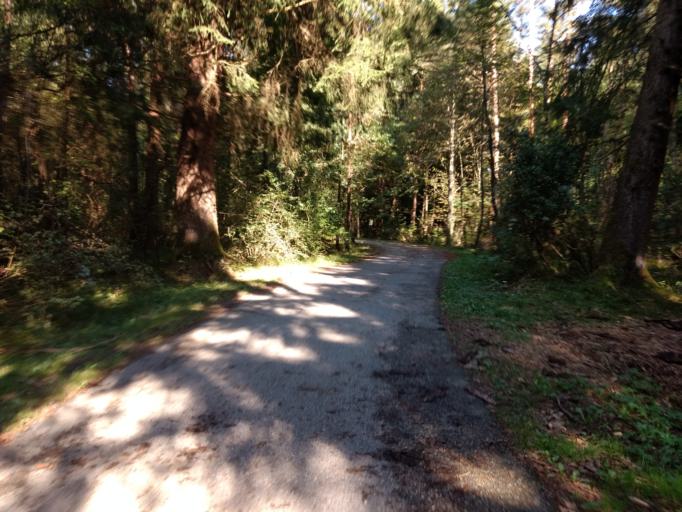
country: DE
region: Bavaria
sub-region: Upper Bavaria
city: Geretsried
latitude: 47.8404
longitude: 11.4805
